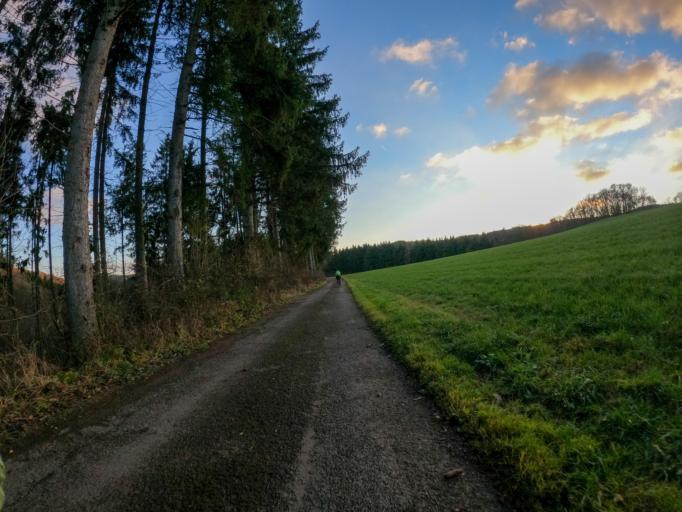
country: LU
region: Diekirch
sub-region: Canton de Wiltz
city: Bavigne
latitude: 49.9186
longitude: 5.8545
